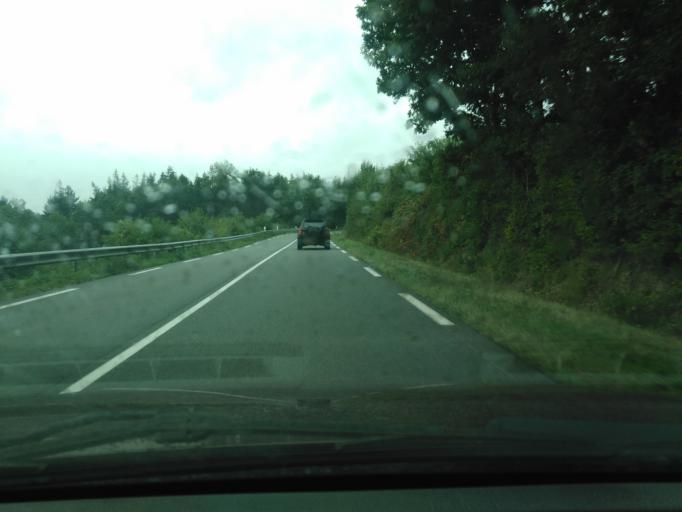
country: FR
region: Pays de la Loire
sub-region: Departement de la Vendee
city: Bournezeau
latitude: 46.5920
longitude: -1.1220
